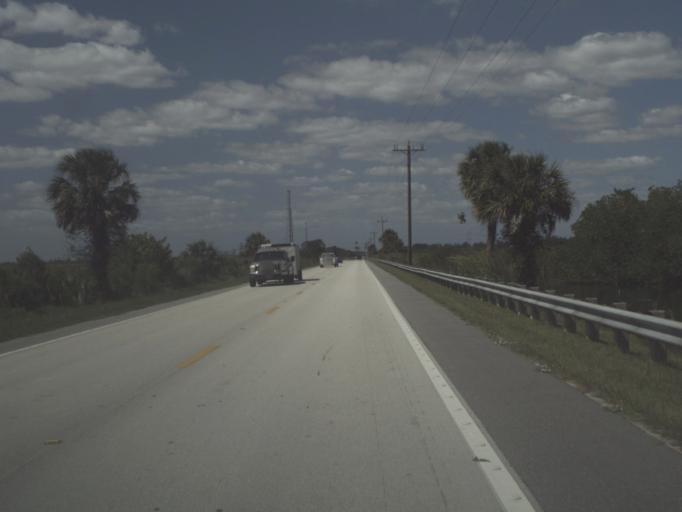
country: US
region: Florida
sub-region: Collier County
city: Marco
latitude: 25.9065
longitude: -81.3520
